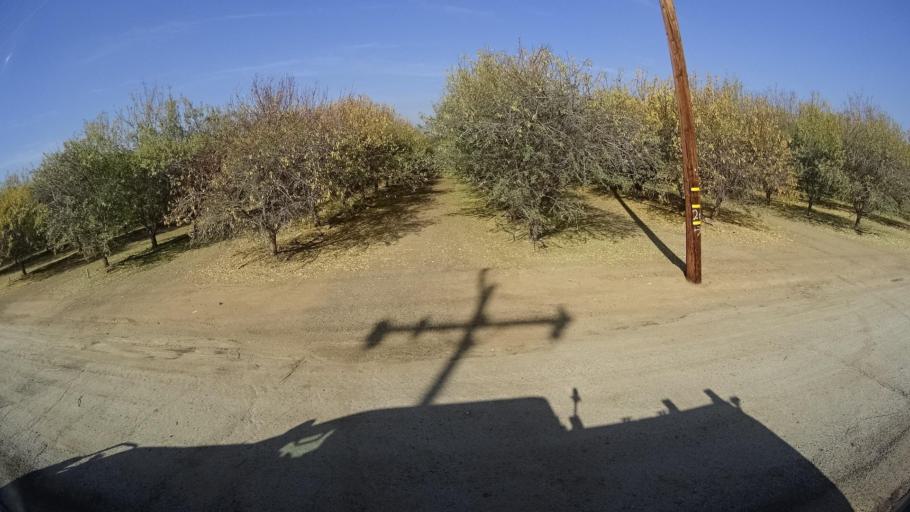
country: US
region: California
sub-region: Kern County
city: McFarland
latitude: 35.6311
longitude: -119.1820
